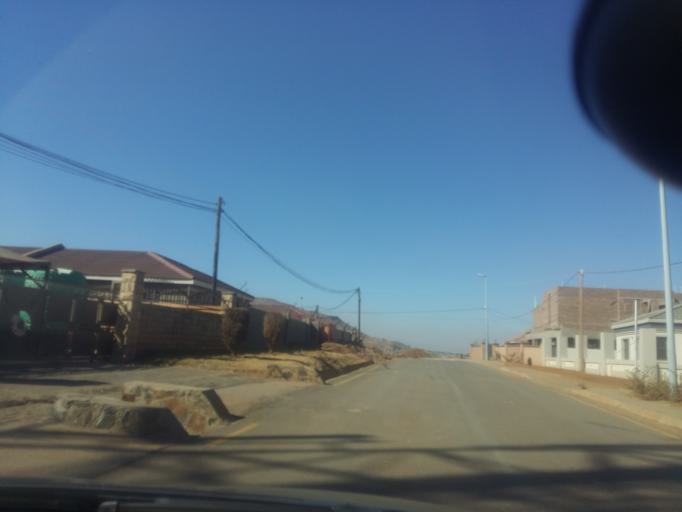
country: LS
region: Maseru
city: Maseru
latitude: -29.3449
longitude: 27.4465
